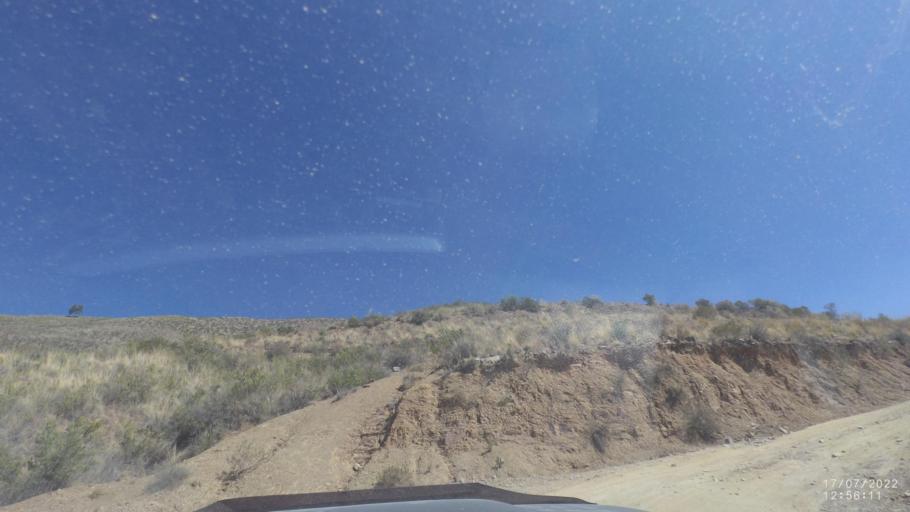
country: BO
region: Cochabamba
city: Tarata
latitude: -17.6599
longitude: -66.1374
